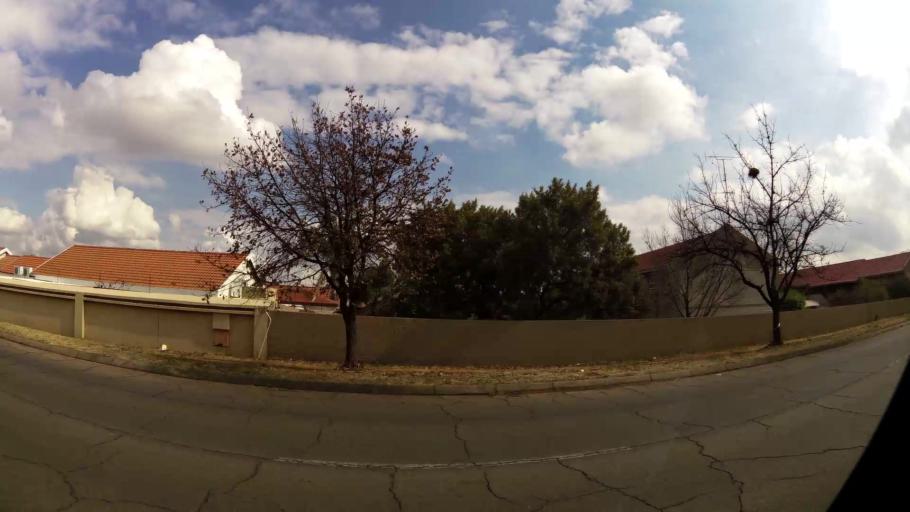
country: ZA
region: Gauteng
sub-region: Sedibeng District Municipality
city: Vanderbijlpark
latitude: -26.7391
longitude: 27.8440
